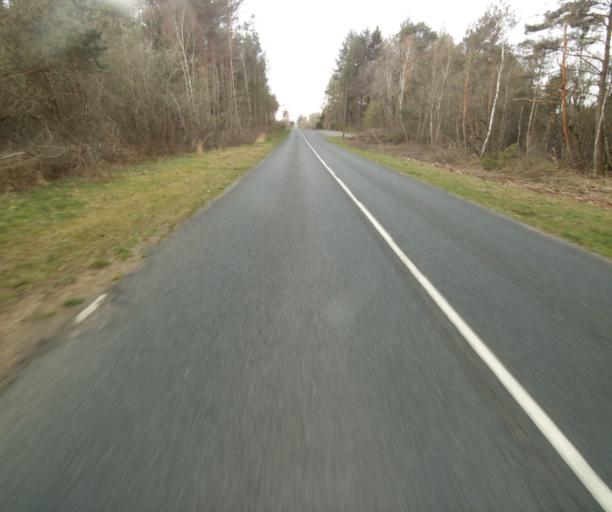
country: FR
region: Limousin
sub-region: Departement de la Correze
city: Egletons
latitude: 45.2763
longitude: 1.9886
